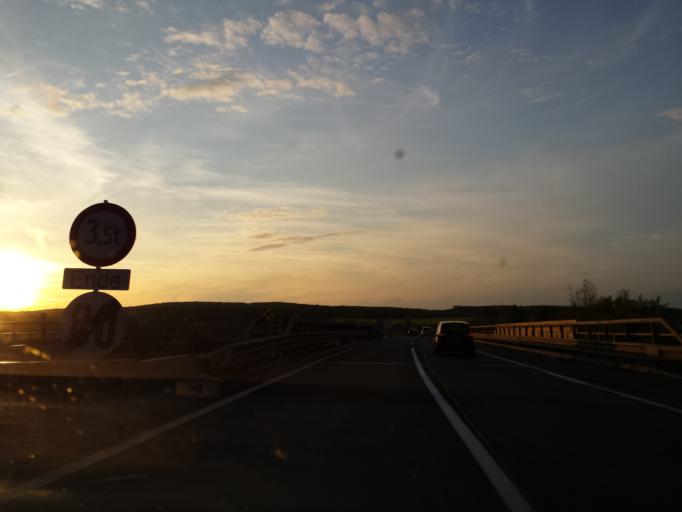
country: AT
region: Burgenland
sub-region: Politischer Bezirk Neusiedl am See
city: Parndorf
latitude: 47.9806
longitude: 16.8401
